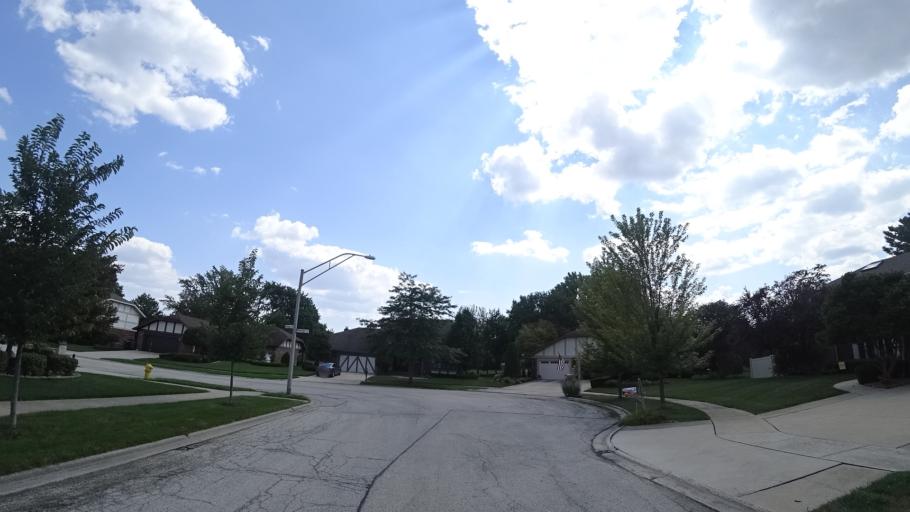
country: US
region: Illinois
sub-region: Cook County
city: Orland Park
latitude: 41.6280
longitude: -87.8239
